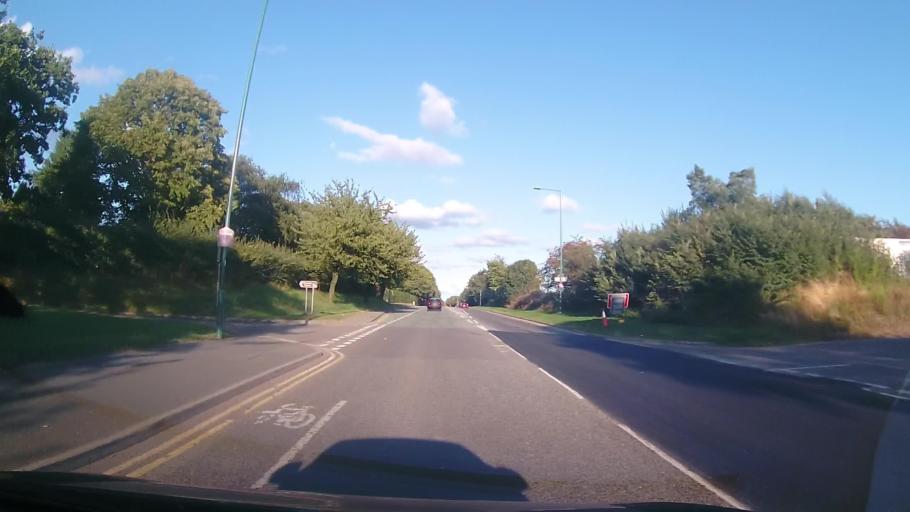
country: GB
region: England
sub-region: Shropshire
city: Shrewsbury
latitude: 52.6886
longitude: -2.7382
